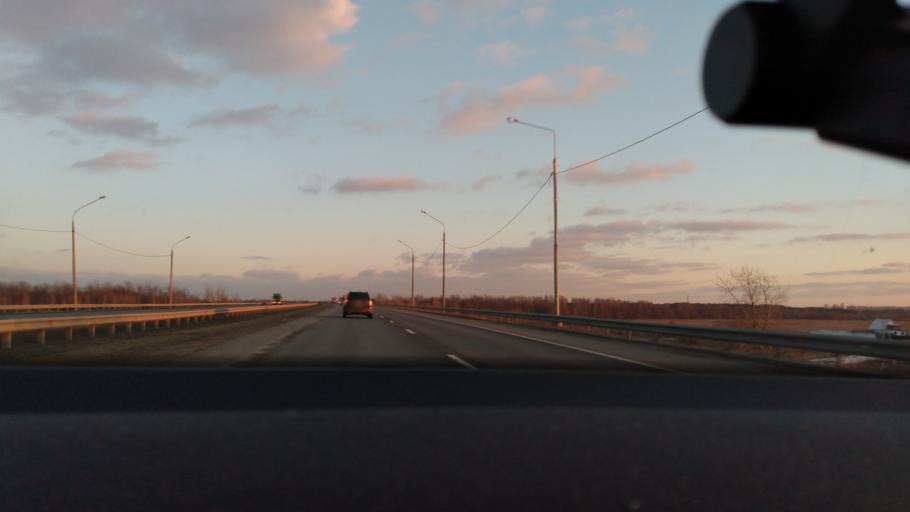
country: RU
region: Moskovskaya
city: Raduzhnyy
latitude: 55.1310
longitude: 38.7788
